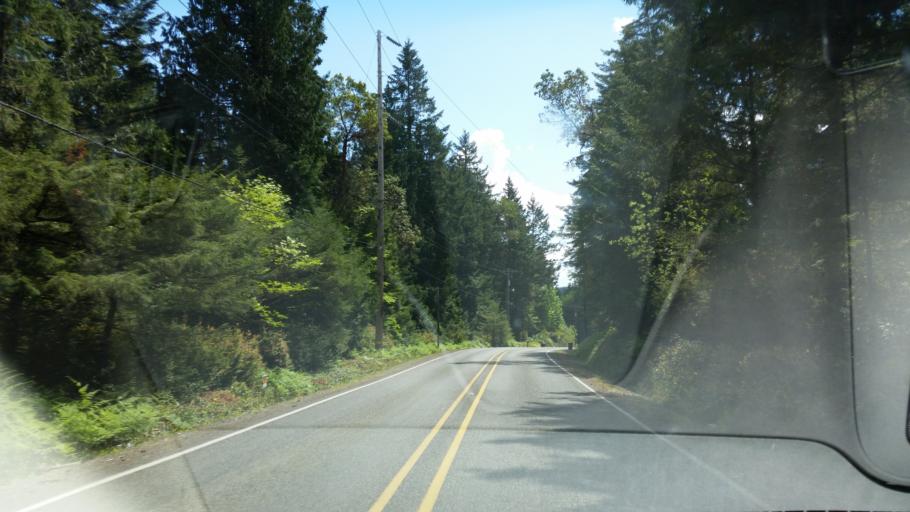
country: US
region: Washington
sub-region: Pierce County
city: Key Center
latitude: 47.3234
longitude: -122.7697
